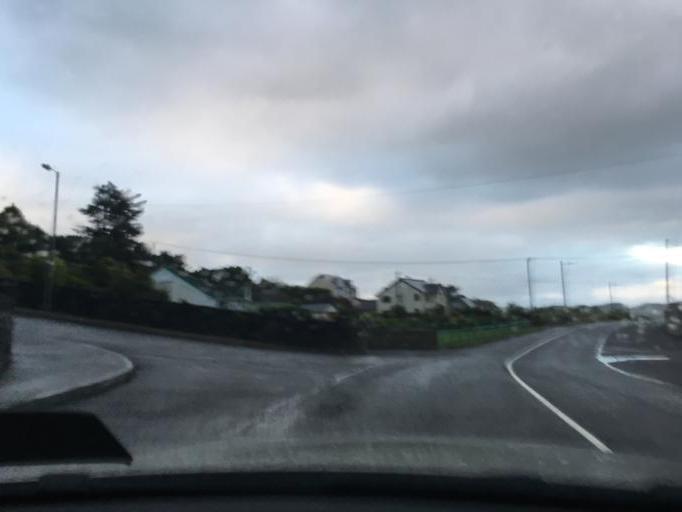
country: IE
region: Ulster
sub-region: County Donegal
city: Killybegs
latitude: 54.6347
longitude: -8.4549
